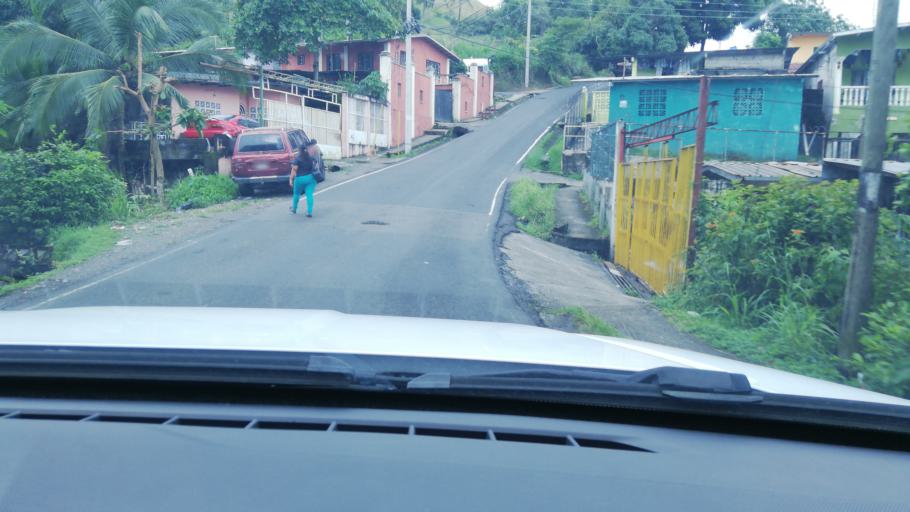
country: PA
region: Panama
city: Las Cumbres
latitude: 9.0710
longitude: -79.5146
